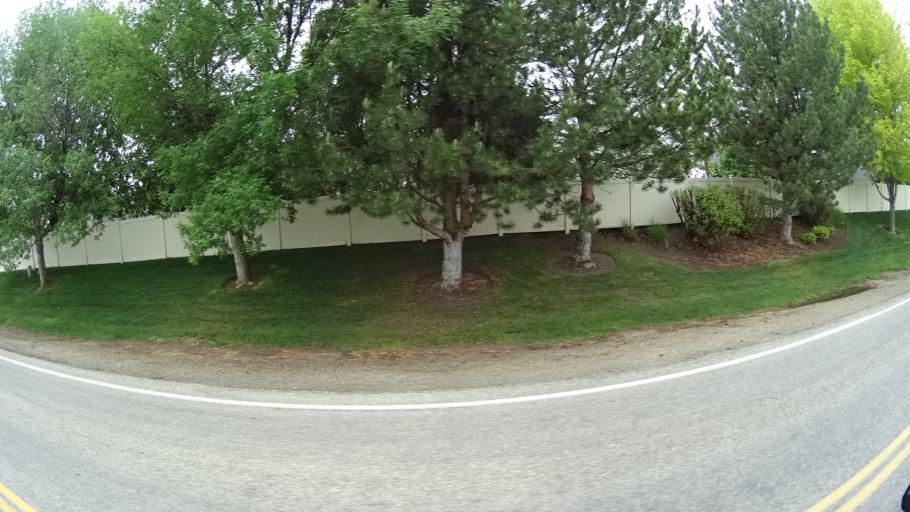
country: US
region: Idaho
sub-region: Ada County
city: Eagle
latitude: 43.7146
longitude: -116.3169
